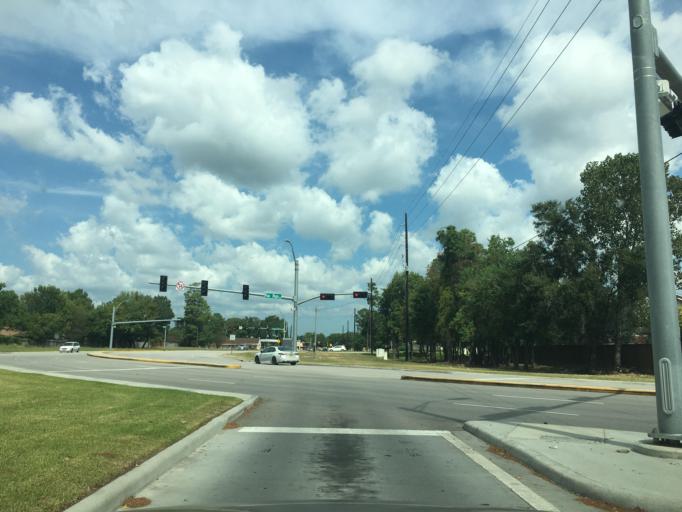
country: US
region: Texas
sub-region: Harris County
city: Spring
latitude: 30.1168
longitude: -95.3960
